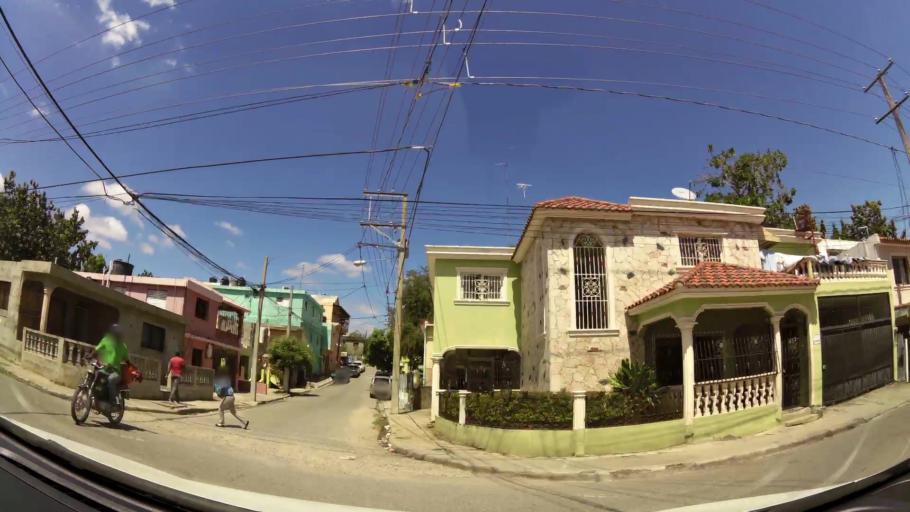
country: DO
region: San Cristobal
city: San Cristobal
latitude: 18.4033
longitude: -70.1086
